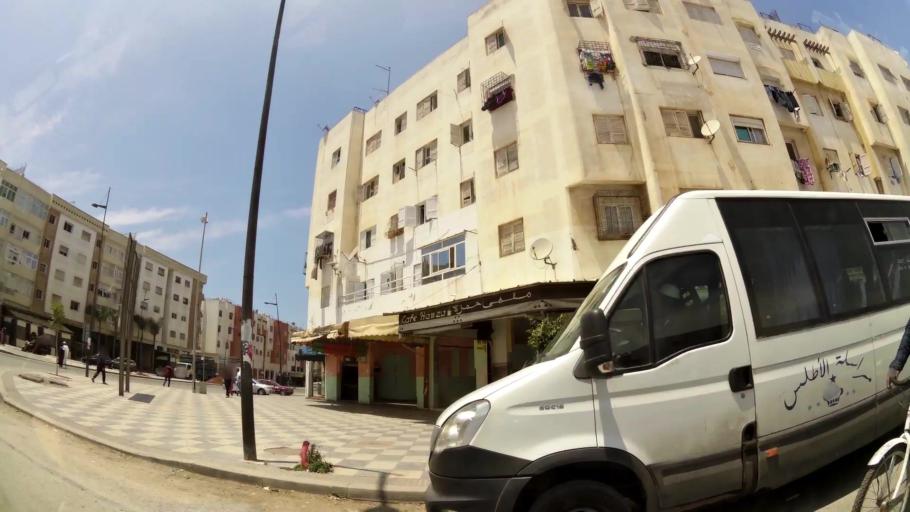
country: MA
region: Rabat-Sale-Zemmour-Zaer
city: Sale
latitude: 34.0623
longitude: -6.7823
